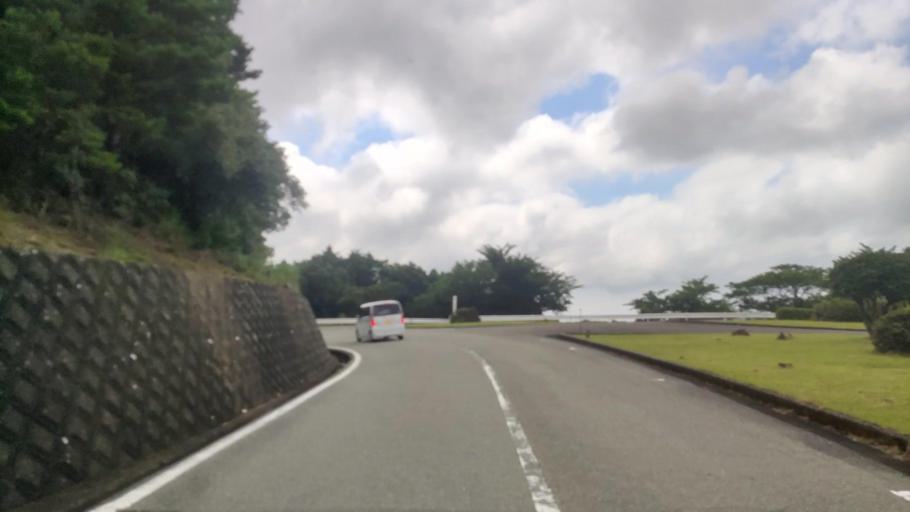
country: JP
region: Mie
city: Toba
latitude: 34.4585
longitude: 136.7916
